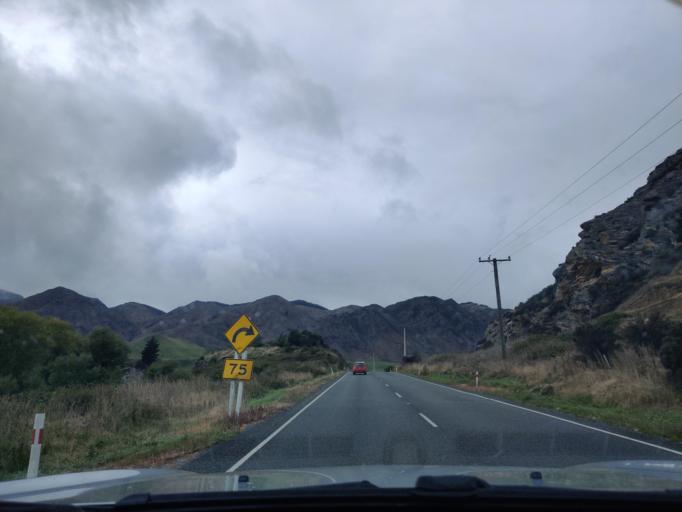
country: NZ
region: Canterbury
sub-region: Hurunui District
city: Amberley
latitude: -42.6282
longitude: 172.7691
